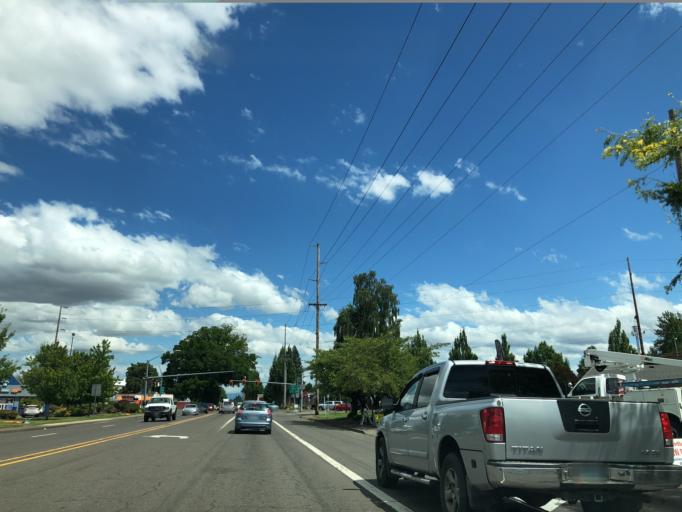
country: US
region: Oregon
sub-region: Marion County
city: Woodburn
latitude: 45.1513
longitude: -122.8329
